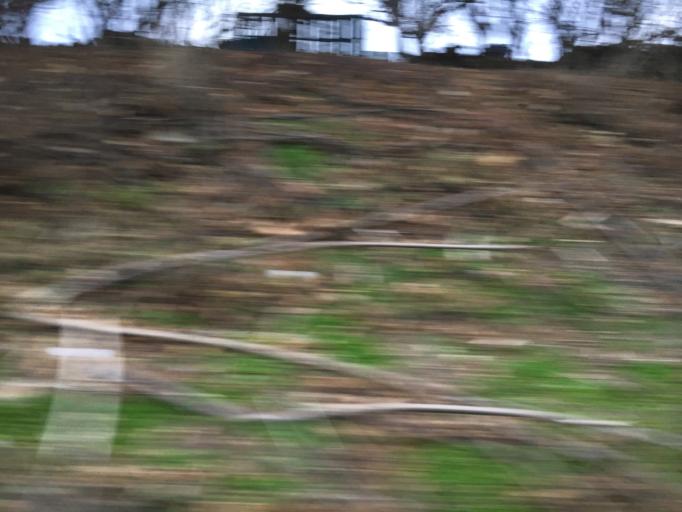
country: US
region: Pennsylvania
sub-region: Lehigh County
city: Schnecksville
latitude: 40.6818
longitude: -75.5807
